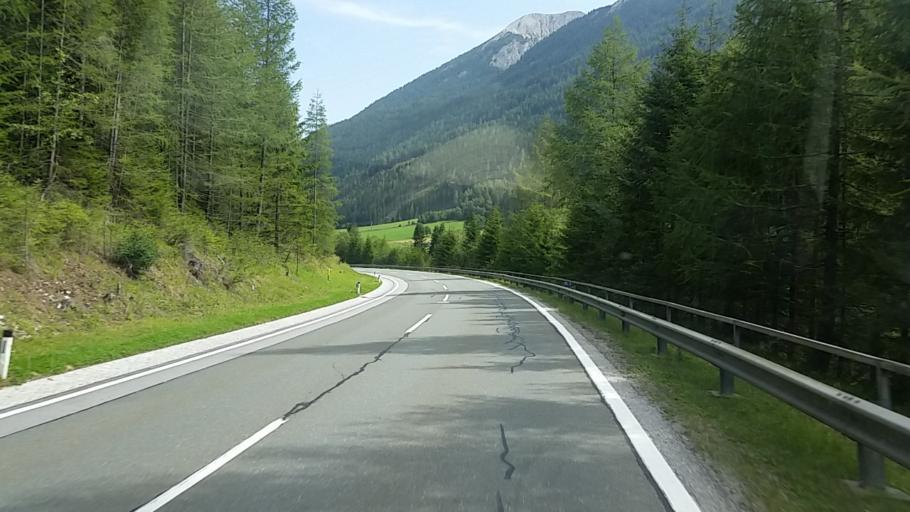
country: AT
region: Salzburg
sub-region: Politischer Bezirk Tamsweg
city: Tweng
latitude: 47.1960
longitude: 13.5928
